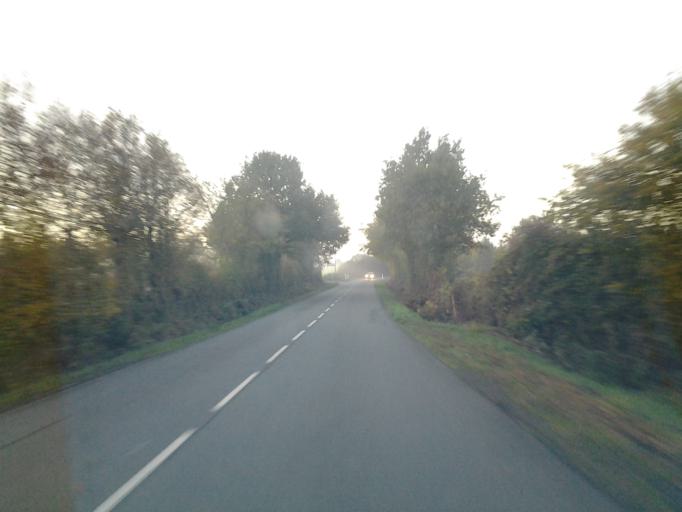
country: FR
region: Pays de la Loire
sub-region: Departement de la Vendee
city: Bournezeau
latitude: 46.6503
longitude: -1.2296
